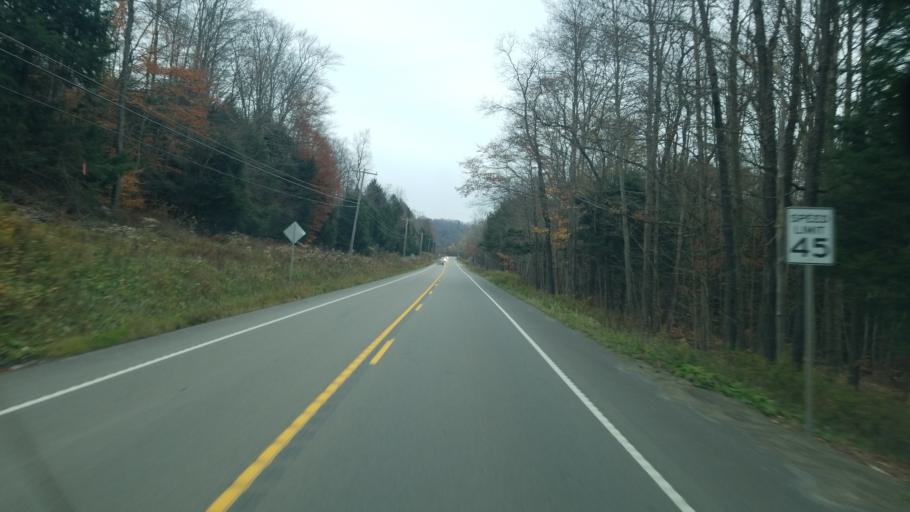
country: US
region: Pennsylvania
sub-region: McKean County
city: Kane
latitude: 41.6361
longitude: -78.8177
